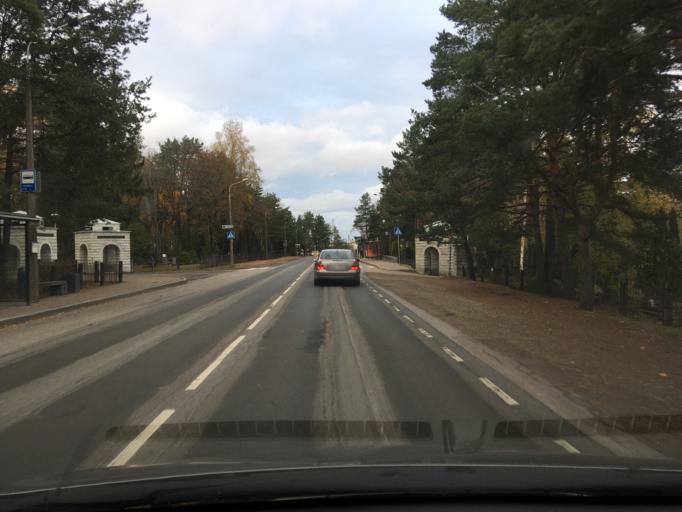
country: EE
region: Harju
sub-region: Tallinna linn
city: Tallinn
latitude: 59.3918
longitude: 24.7086
